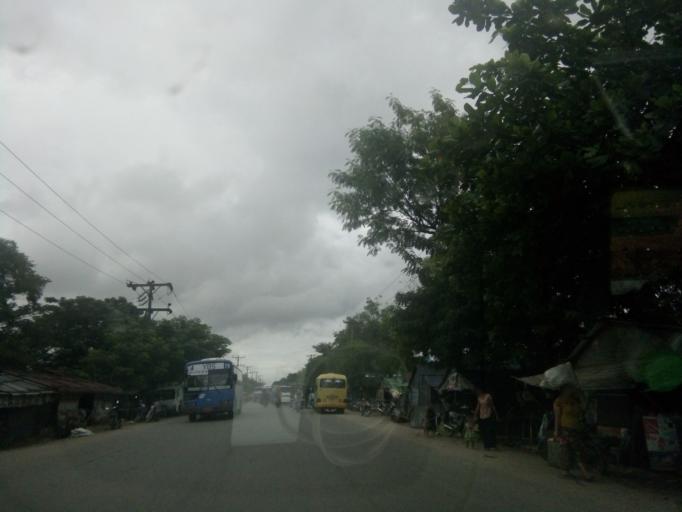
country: MM
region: Yangon
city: Yangon
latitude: 16.9163
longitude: 96.0528
